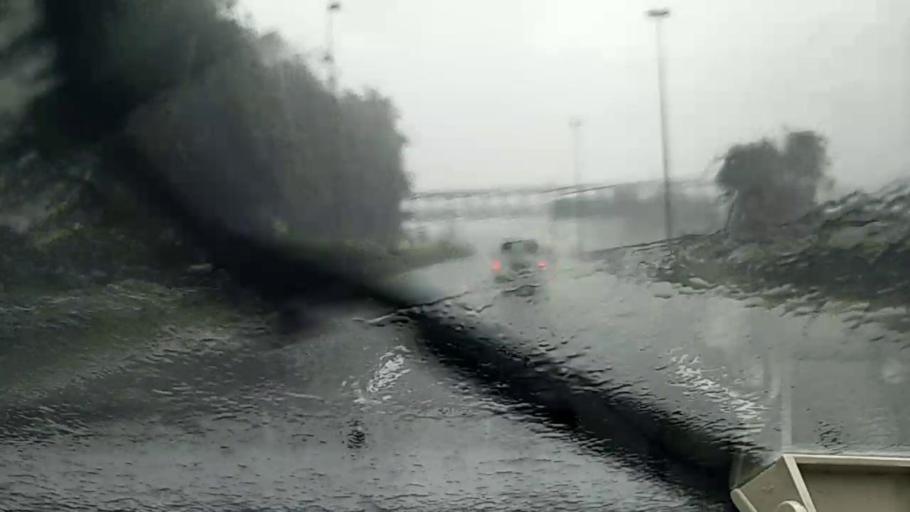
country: MY
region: Selangor
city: Kampong Baharu Balakong
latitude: 2.9828
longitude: 101.7633
